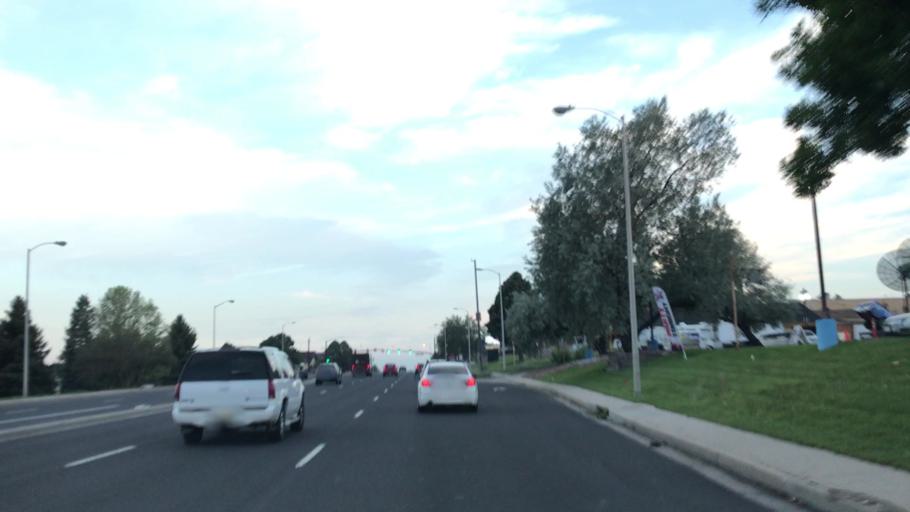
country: US
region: Colorado
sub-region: El Paso County
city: Cimarron Hills
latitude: 38.8792
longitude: -104.7572
